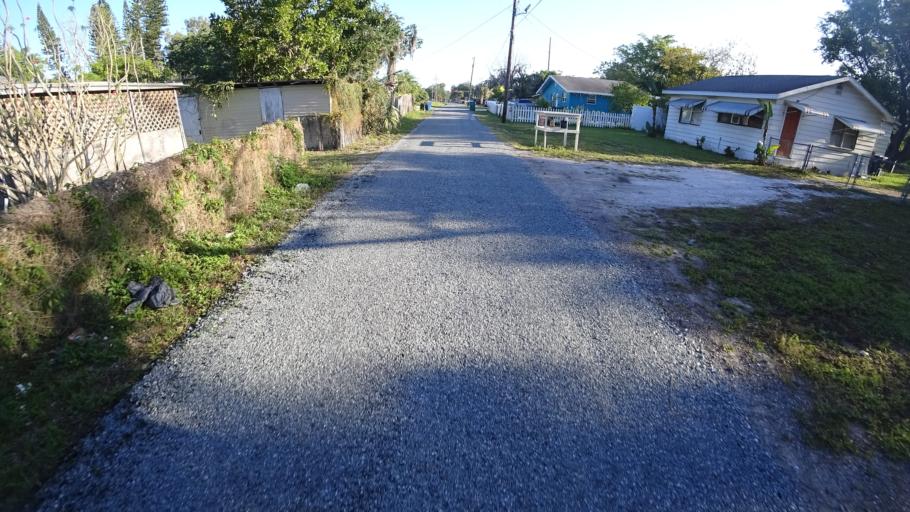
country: US
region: Florida
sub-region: Manatee County
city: Samoset
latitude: 27.4459
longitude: -82.5362
